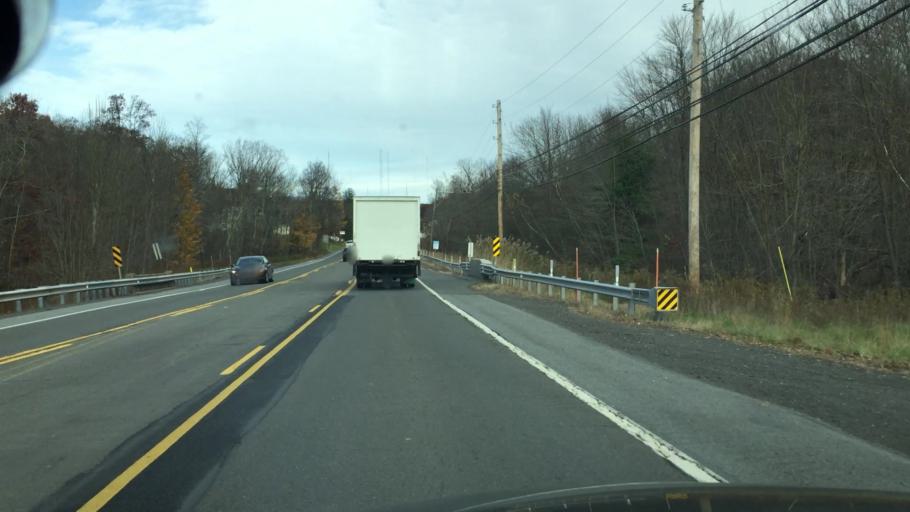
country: US
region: Pennsylvania
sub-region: Luzerne County
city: Mountain Top
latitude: 41.1481
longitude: -75.8972
